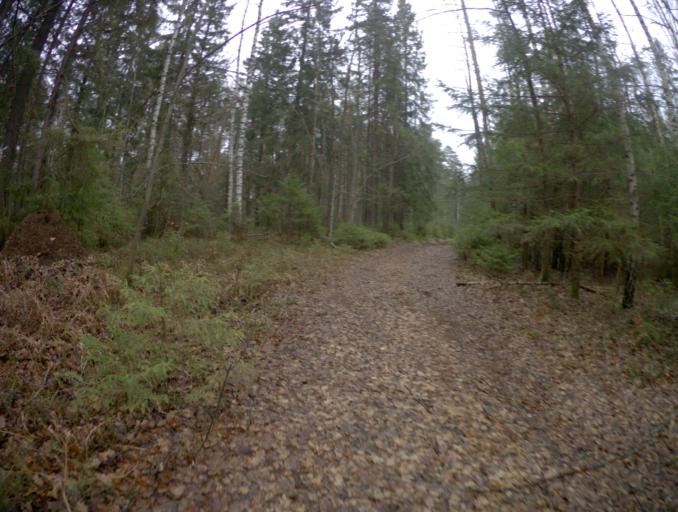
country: RU
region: Vladimir
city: Golovino
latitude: 56.0152
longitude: 40.5264
